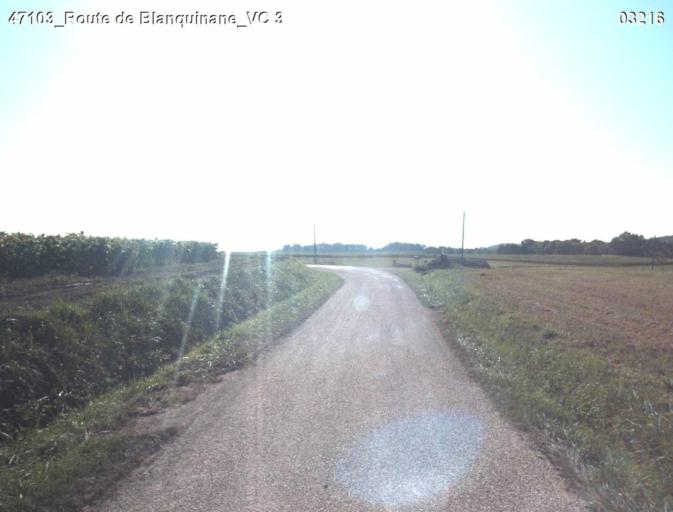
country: FR
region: Aquitaine
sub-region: Departement du Lot-et-Garonne
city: Nerac
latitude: 44.0900
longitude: 0.3279
